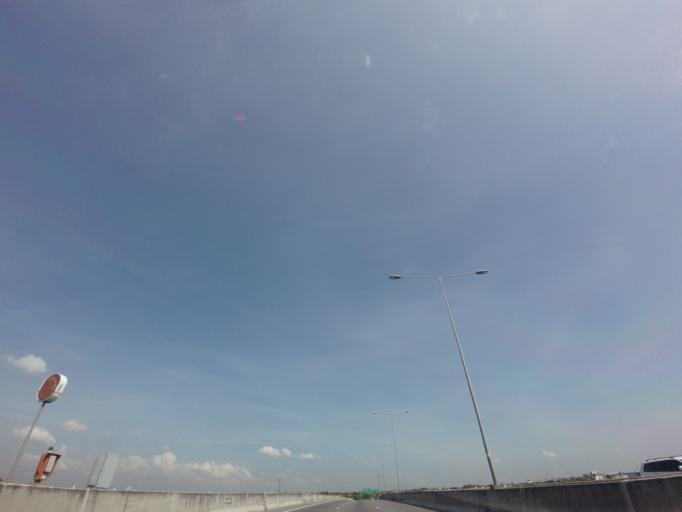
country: TH
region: Bangkok
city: Bang Khen
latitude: 13.8755
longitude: 100.6466
